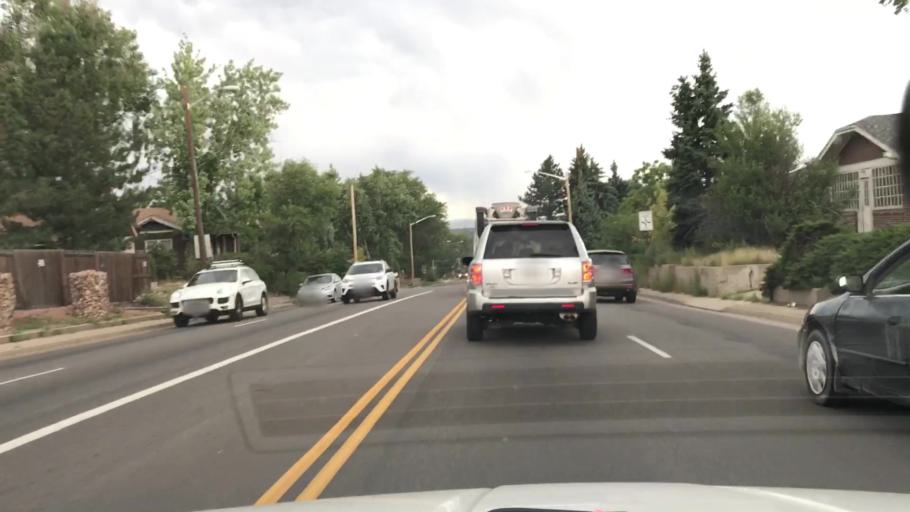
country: US
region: Colorado
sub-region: Jefferson County
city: Edgewater
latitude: 39.7620
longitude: -105.0533
